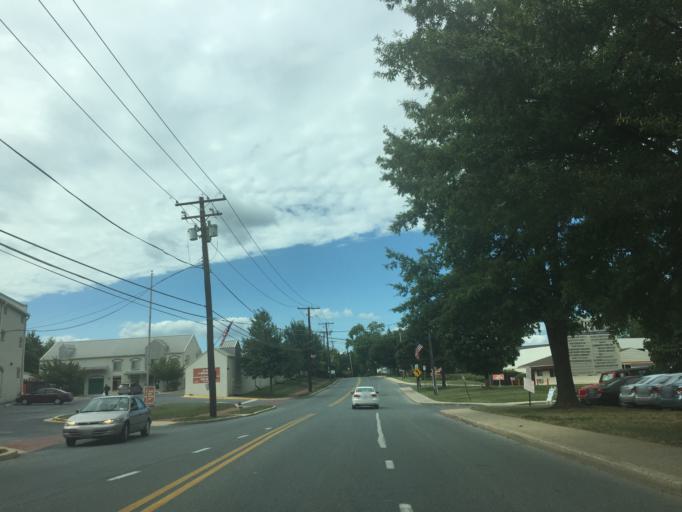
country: US
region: Maryland
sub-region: Montgomery County
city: Gaithersburg
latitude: 39.1406
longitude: -77.1843
